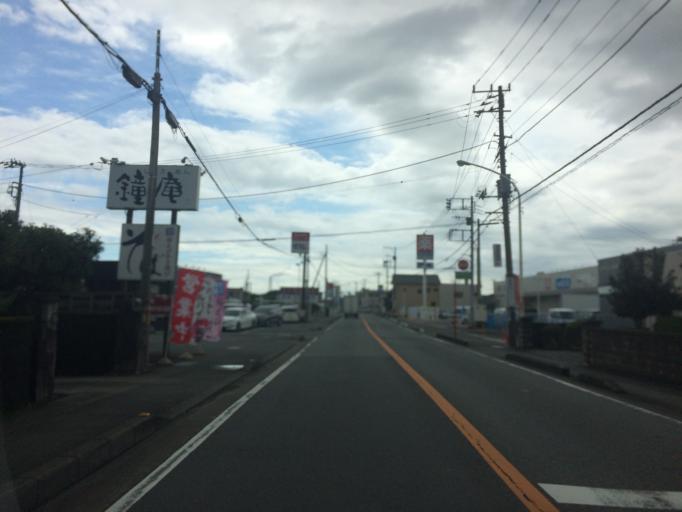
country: JP
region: Shizuoka
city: Fuji
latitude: 35.1704
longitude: 138.6485
